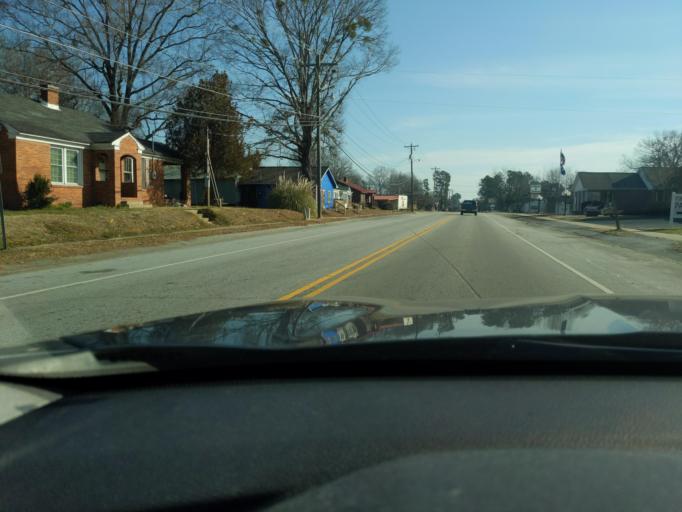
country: US
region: South Carolina
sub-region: Abbeville County
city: Calhoun Falls
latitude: 34.0900
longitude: -82.5873
